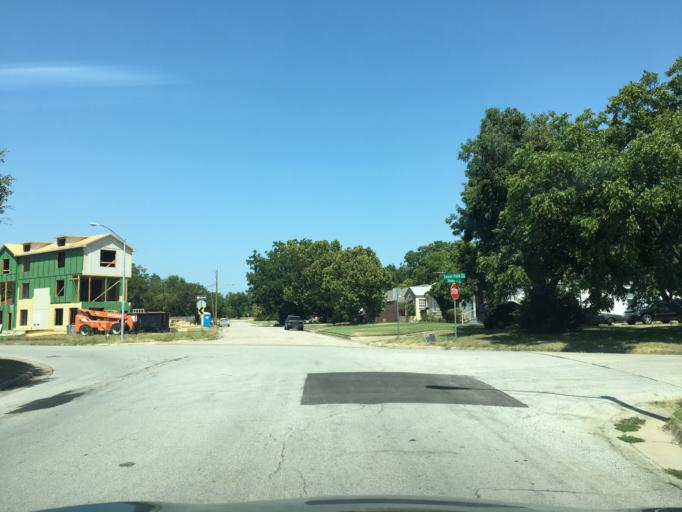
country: US
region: Texas
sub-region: Tarrant County
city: Fort Worth
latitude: 32.7026
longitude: -97.3526
